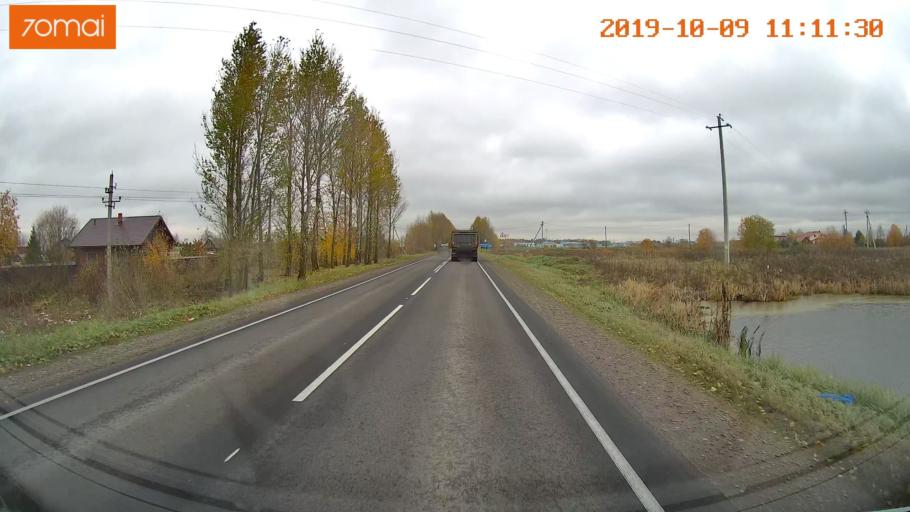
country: RU
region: Vologda
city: Vologda
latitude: 59.1685
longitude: 39.8211
